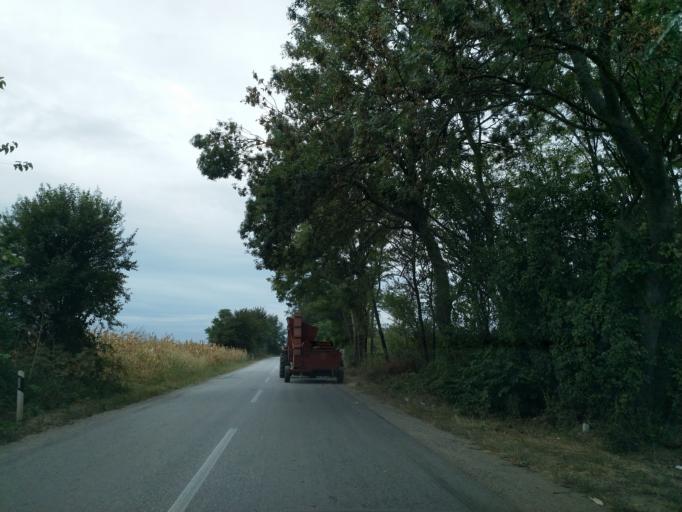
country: RS
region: Central Serbia
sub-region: Pomoravski Okrug
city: Paracin
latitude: 43.8400
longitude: 21.3732
